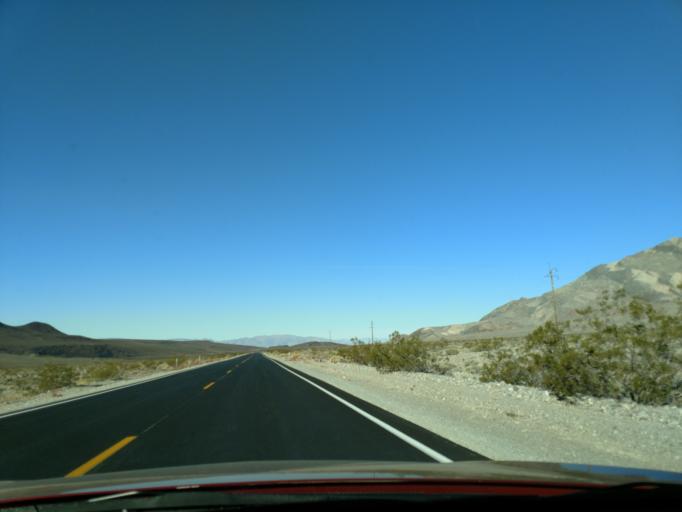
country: US
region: Nevada
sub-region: Nye County
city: Beatty
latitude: 36.3429
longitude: -116.6061
